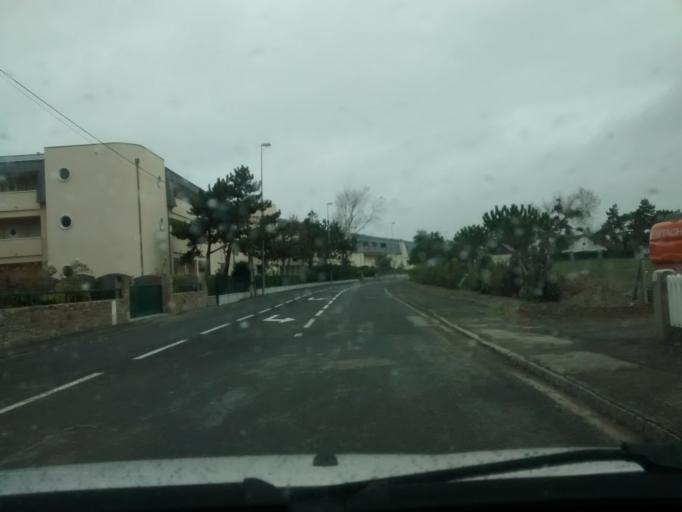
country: FR
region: Lower Normandy
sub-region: Departement de la Manche
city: Jullouville
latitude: 48.7841
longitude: -1.5675
